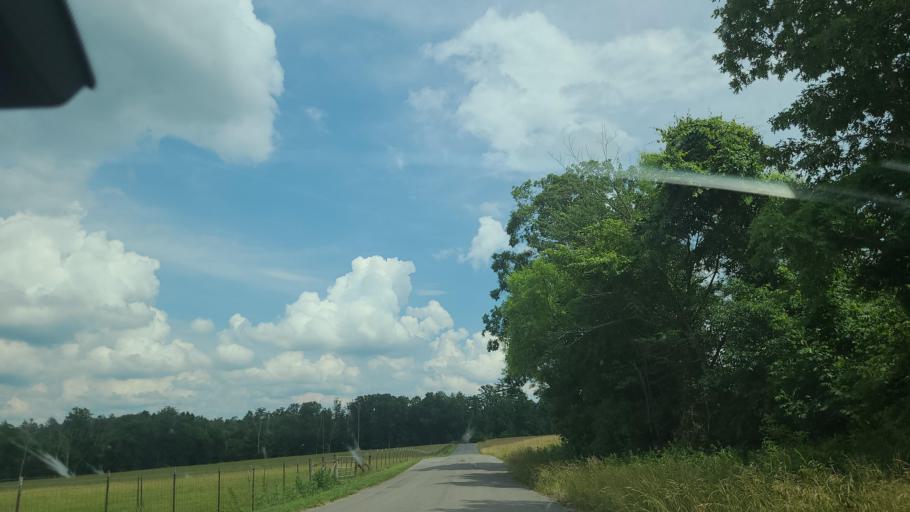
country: US
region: Tennessee
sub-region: Cumberland County
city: Lake Tansi
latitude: 35.7711
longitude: -85.0573
